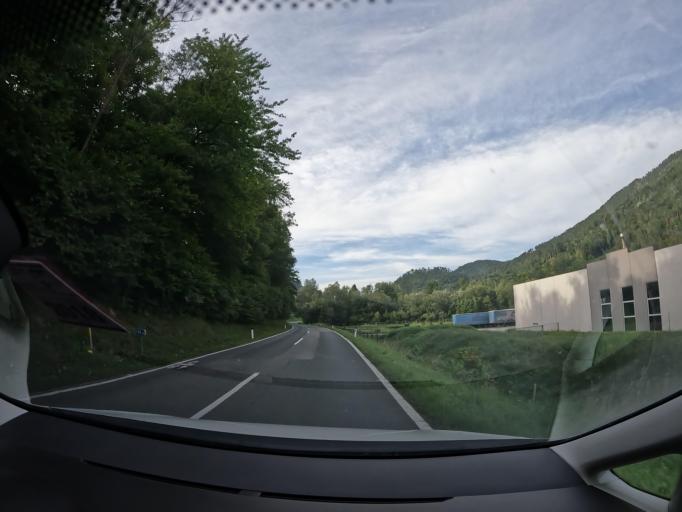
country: AT
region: Carinthia
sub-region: Politischer Bezirk Volkermarkt
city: Bad Eisenkappel
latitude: 46.5001
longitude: 14.5774
